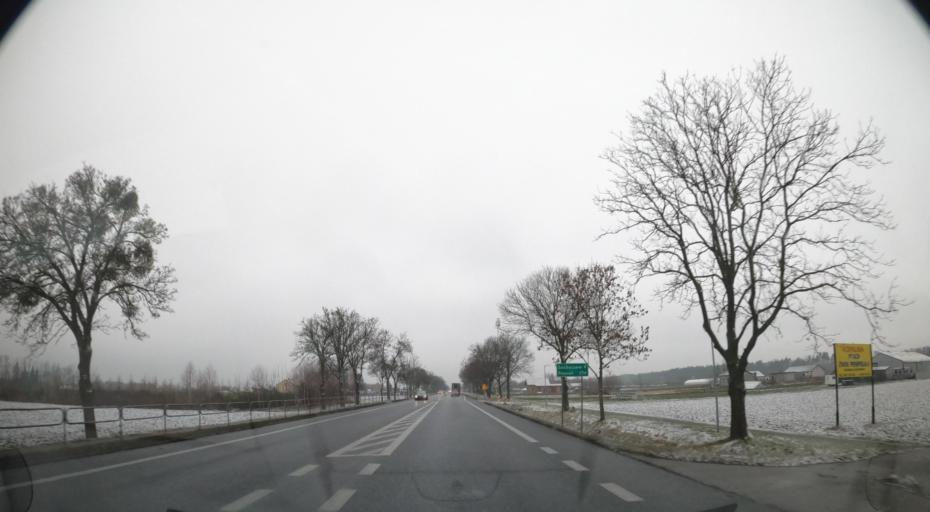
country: PL
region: Masovian Voivodeship
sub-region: Powiat sochaczewski
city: Sochaczew
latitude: 52.2229
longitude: 20.3099
